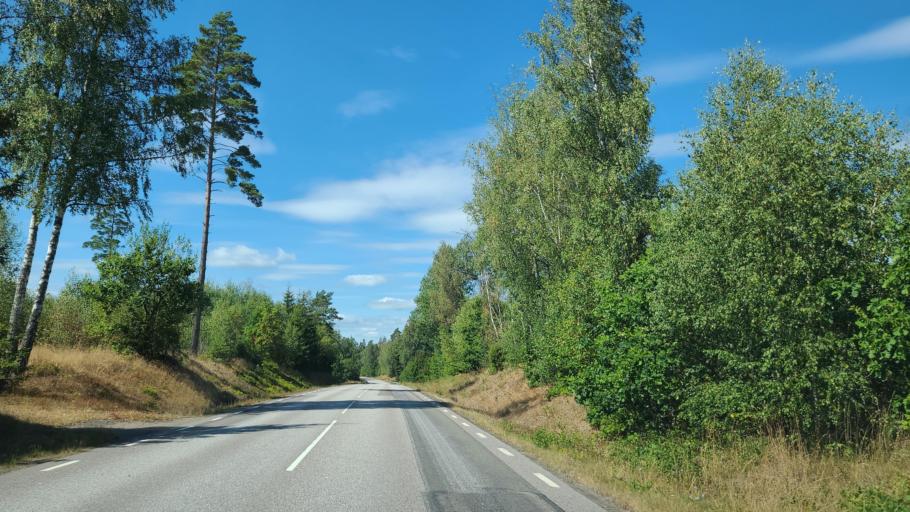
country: SE
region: Kalmar
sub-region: Emmaboda Kommun
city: Emmaboda
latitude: 56.5566
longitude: 15.7412
